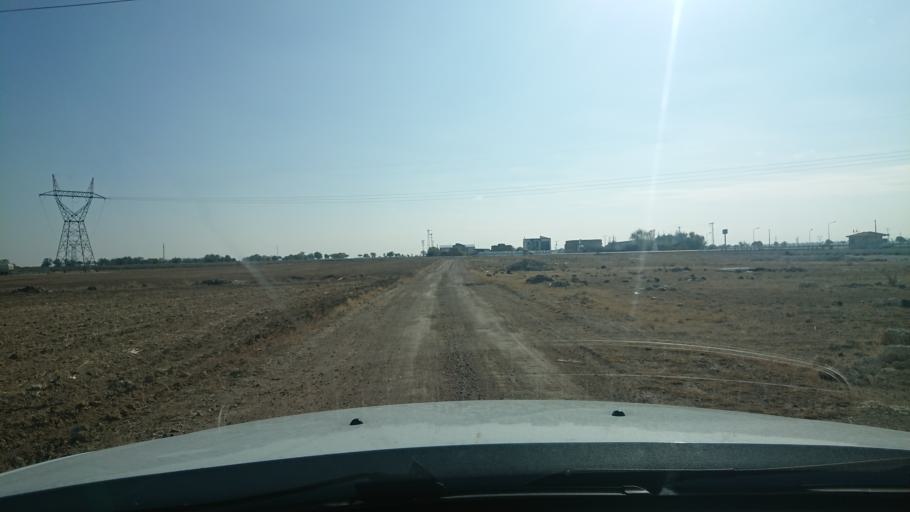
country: TR
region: Aksaray
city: Sultanhani
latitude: 38.2541
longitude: 33.4718
